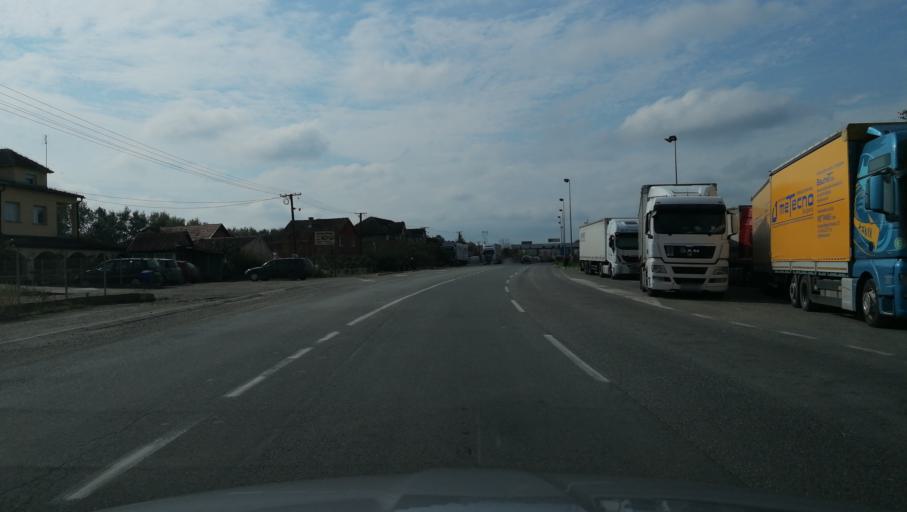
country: RS
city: Visnjicevo
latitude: 44.9177
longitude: 19.3075
